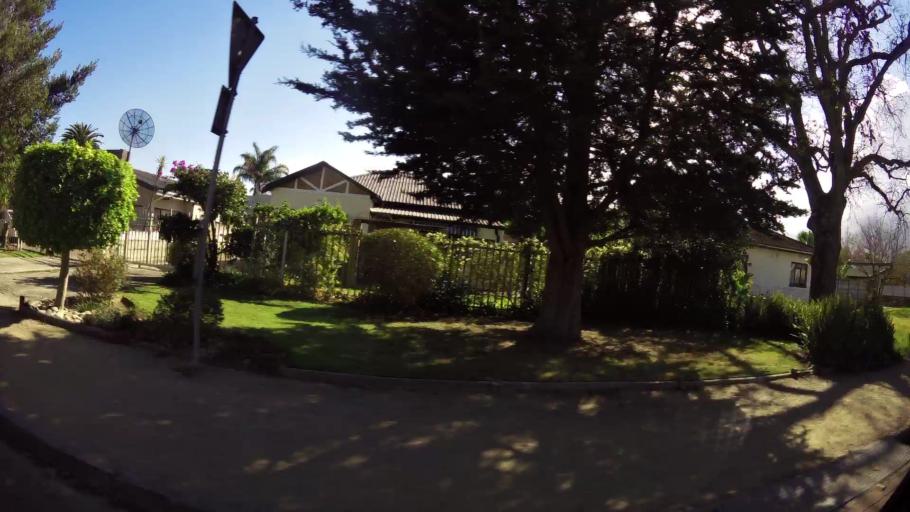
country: ZA
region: Western Cape
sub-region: Eden District Municipality
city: George
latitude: -33.9672
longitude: 22.4545
